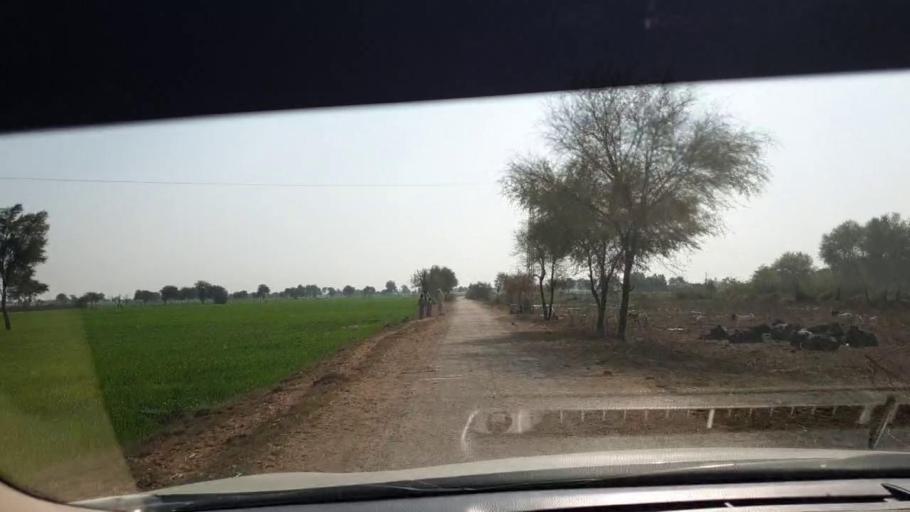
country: PK
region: Sindh
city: Berani
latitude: 25.8112
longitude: 68.7577
